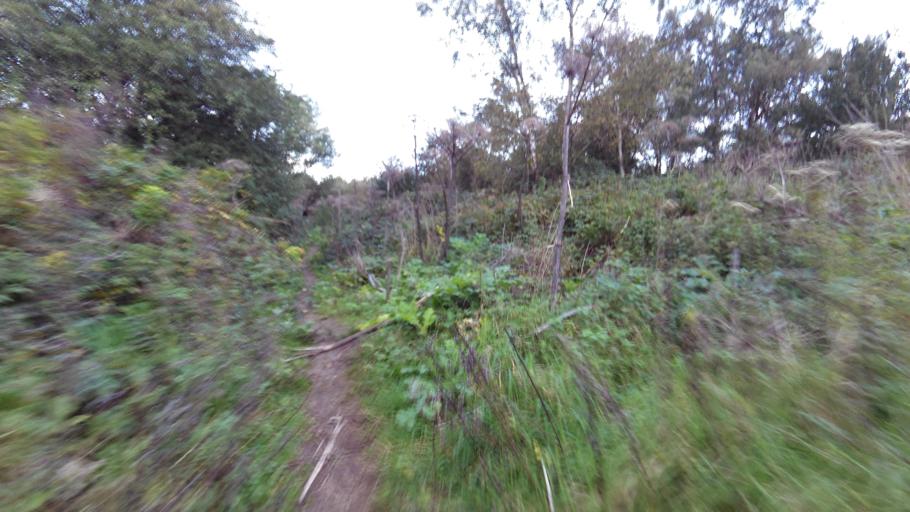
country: NL
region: Gelderland
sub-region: Gemeente Ede
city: Lunteren
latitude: 52.0984
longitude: 5.6590
